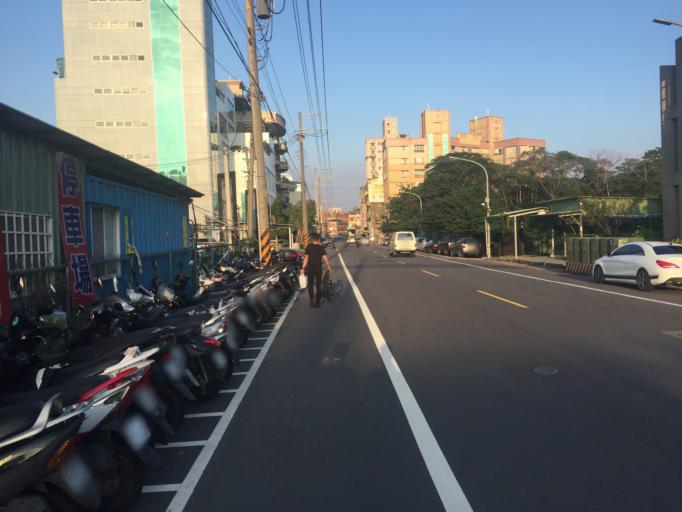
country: TW
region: Taiwan
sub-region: Taoyuan
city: Taoyuan
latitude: 24.9879
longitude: 121.3150
